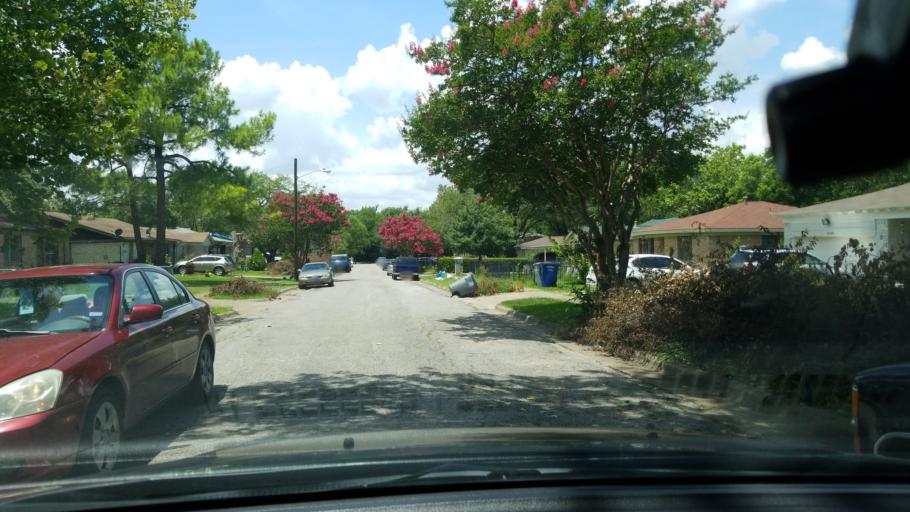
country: US
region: Texas
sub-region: Dallas County
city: Balch Springs
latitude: 32.7365
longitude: -96.6496
